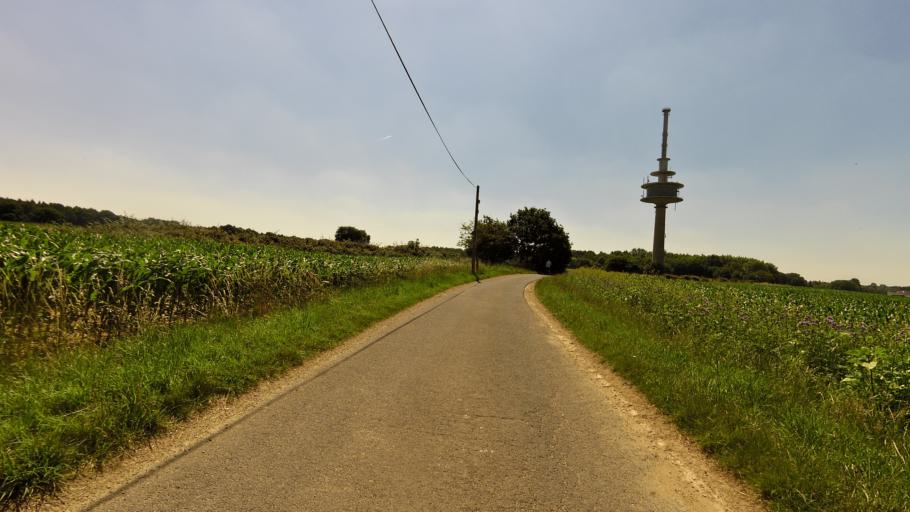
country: DE
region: North Rhine-Westphalia
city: Meckenheim
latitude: 50.6735
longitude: 7.0283
